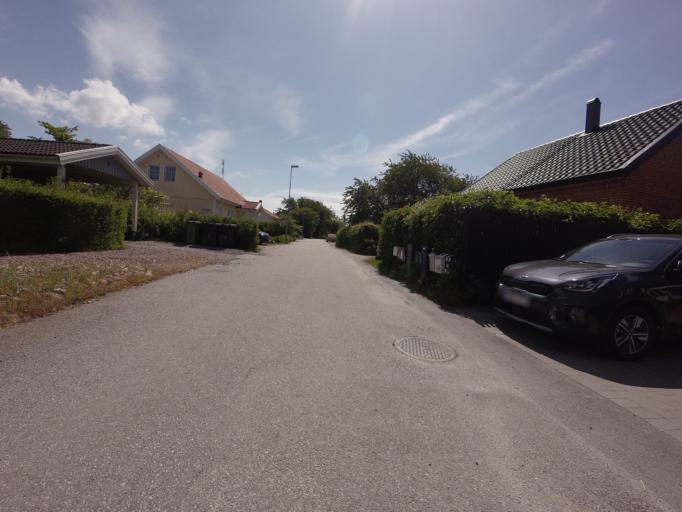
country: SE
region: Skane
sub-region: Trelleborgs Kommun
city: Skare
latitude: 55.3968
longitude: 13.1014
